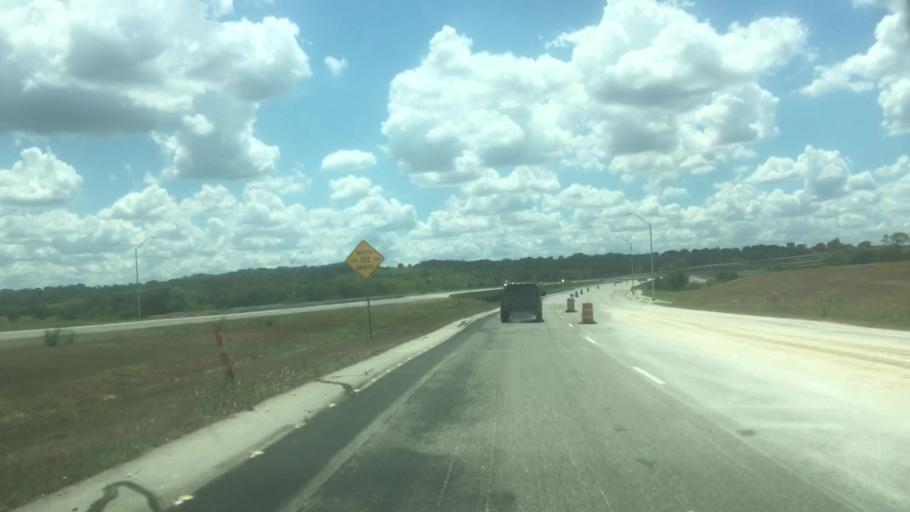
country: US
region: Texas
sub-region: Caldwell County
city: Lockhart
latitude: 29.8627
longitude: -97.7080
